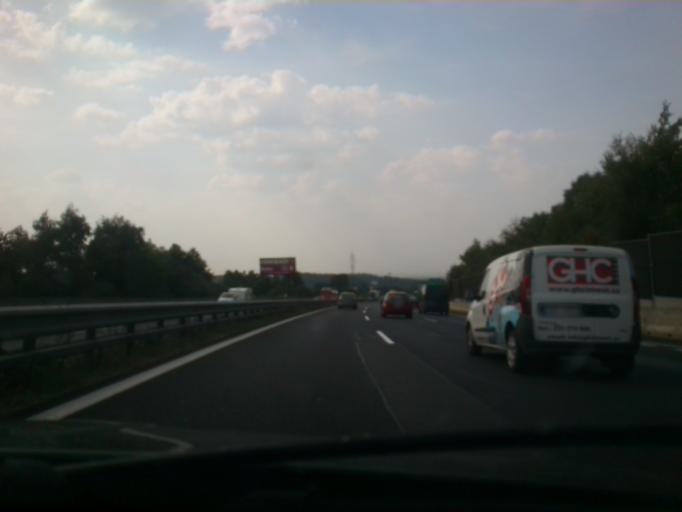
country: CZ
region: Central Bohemia
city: Velke Popovice
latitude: 49.9464
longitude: 14.6501
